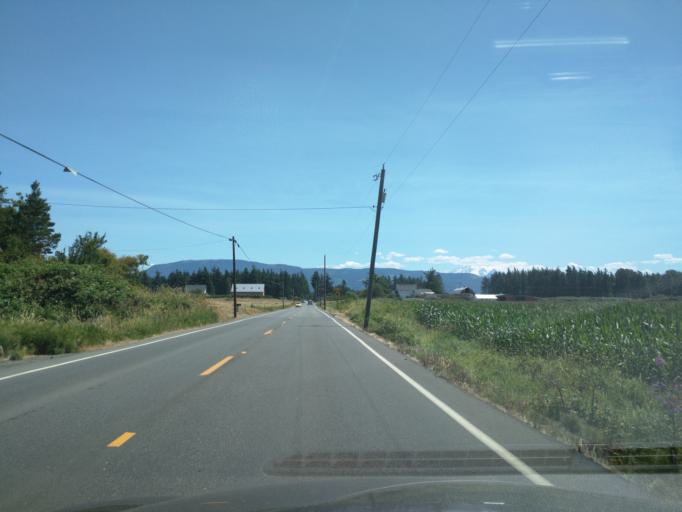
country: US
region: Washington
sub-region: Whatcom County
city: Everson
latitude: 48.8916
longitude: -122.4020
